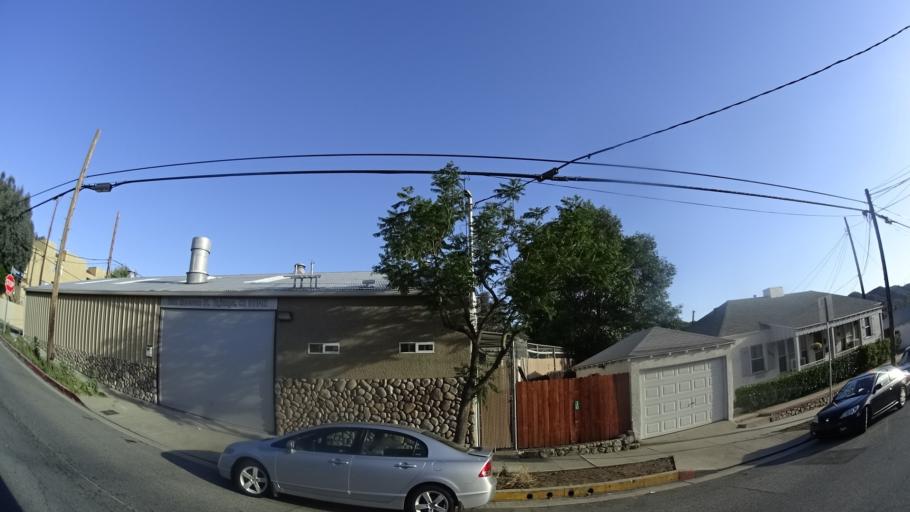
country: US
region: California
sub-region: Los Angeles County
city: La Crescenta-Montrose
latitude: 34.2560
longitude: -118.2981
